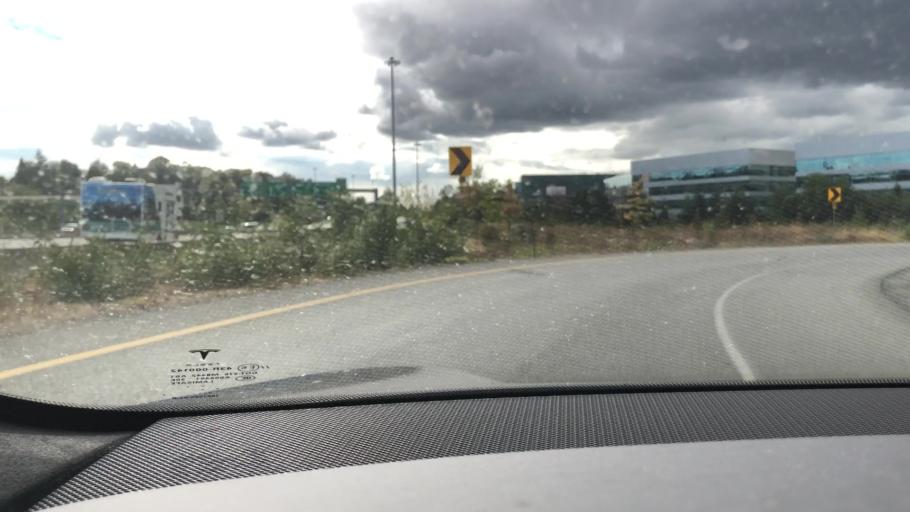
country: CA
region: British Columbia
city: Burnaby
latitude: 49.2581
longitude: -123.0050
